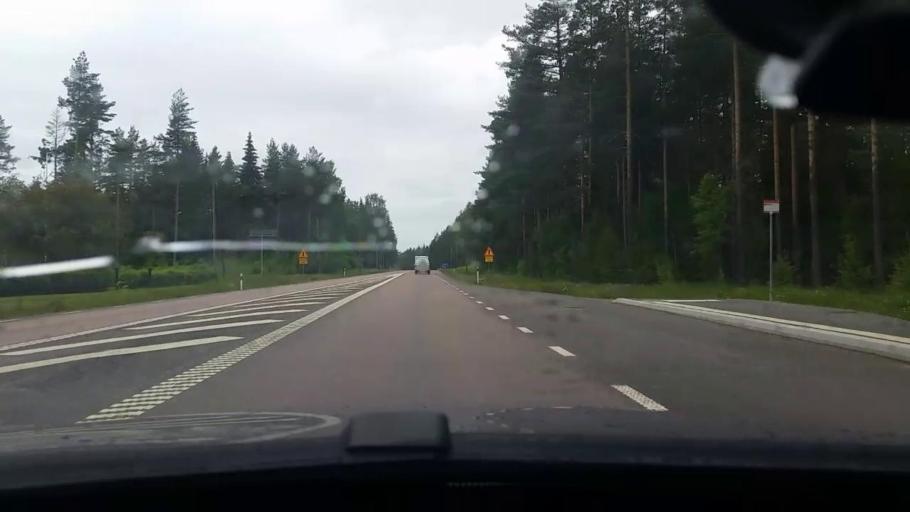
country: SE
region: Dalarna
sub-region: Borlange Kommun
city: Borlaenge
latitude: 60.5295
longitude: 15.3303
